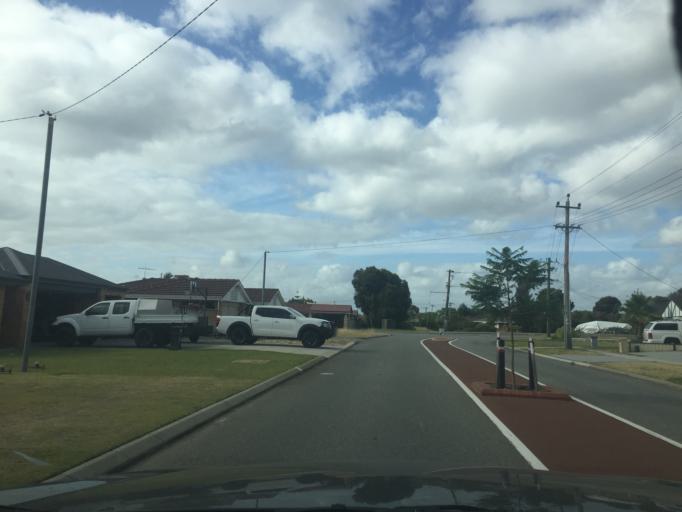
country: AU
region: Western Australia
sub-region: Canning
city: Ferndale
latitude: -32.0445
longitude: 115.9098
